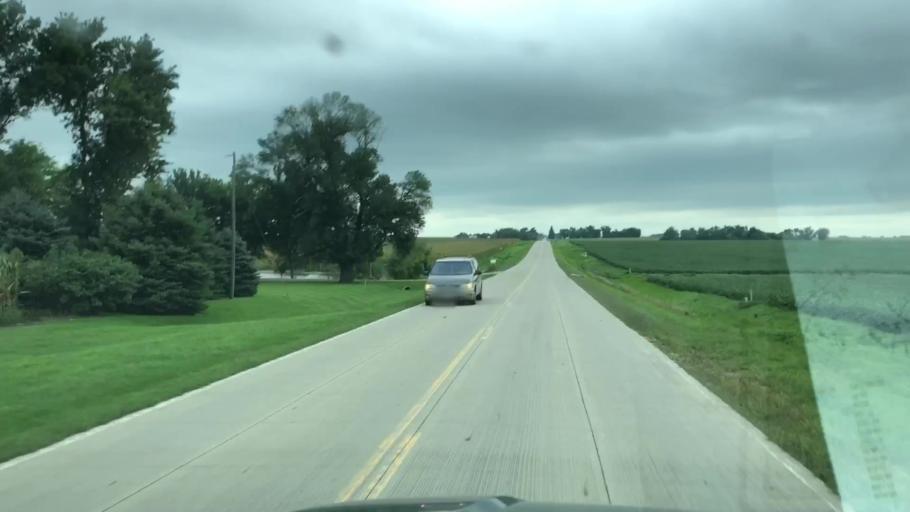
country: US
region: Iowa
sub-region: Sioux County
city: Alton
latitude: 43.1205
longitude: -95.9789
